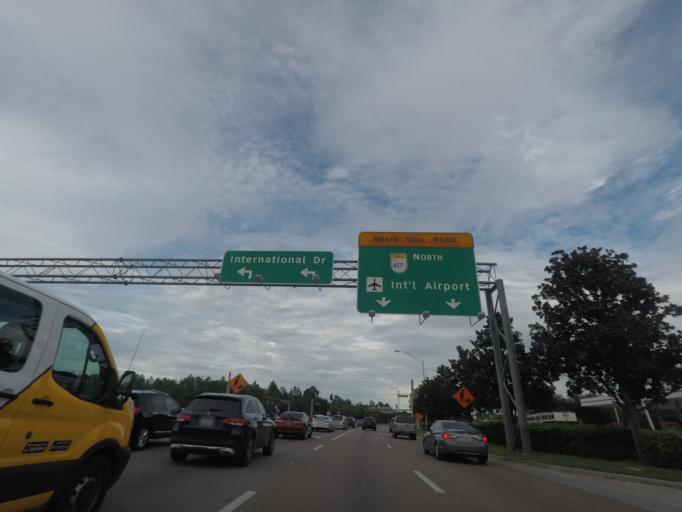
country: US
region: Florida
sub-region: Osceola County
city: Celebration
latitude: 28.3581
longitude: -81.4884
